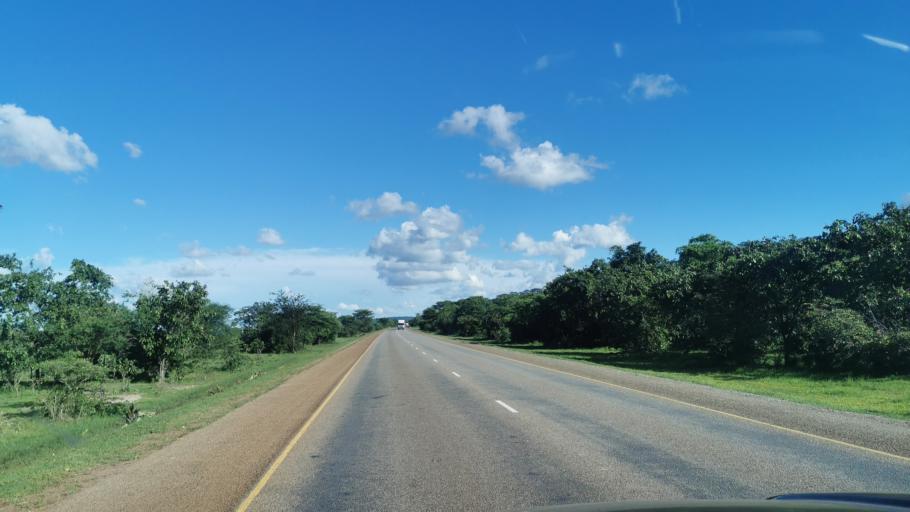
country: TZ
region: Geita
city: Masumbwe
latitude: -3.7176
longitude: 32.2916
